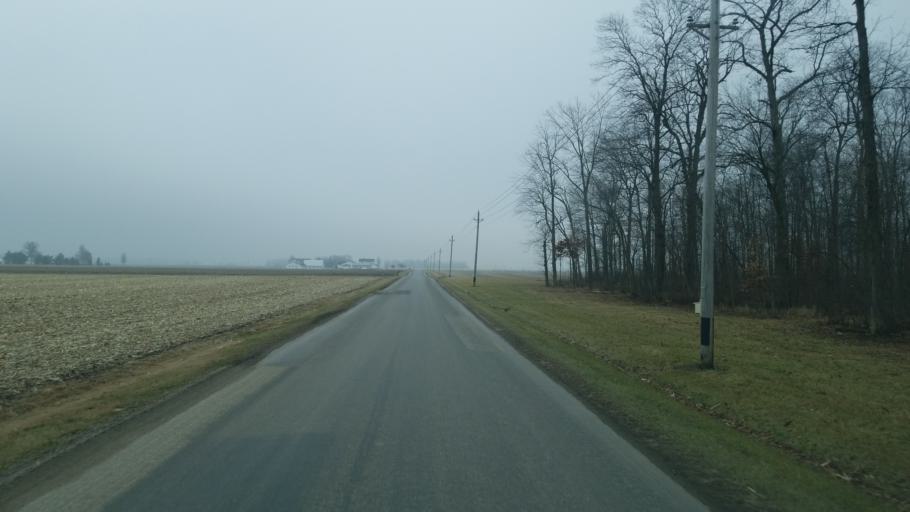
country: US
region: Indiana
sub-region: Adams County
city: Berne
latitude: 40.7000
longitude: -85.0040
